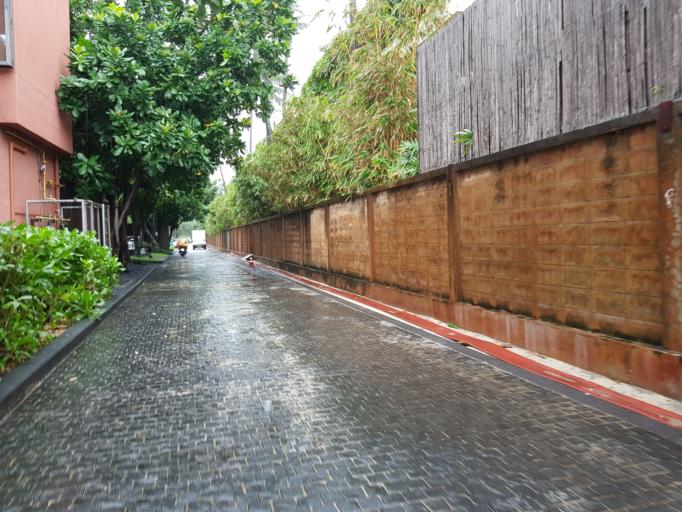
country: TH
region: Surat Thani
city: Ko Samui
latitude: 9.5619
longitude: 100.0257
